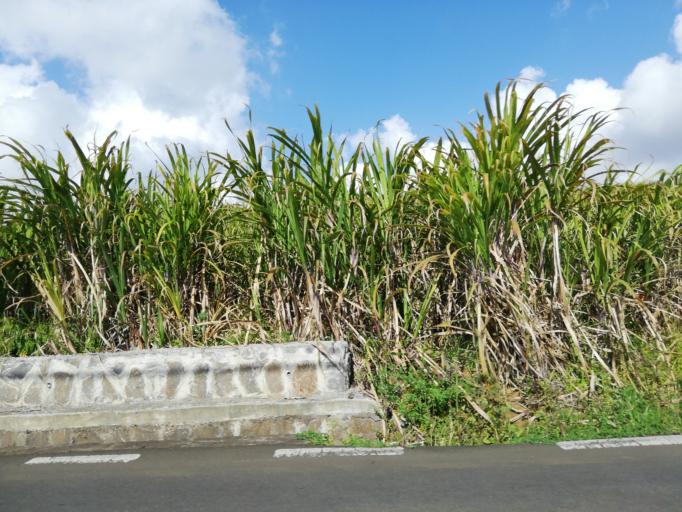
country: MU
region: Pamplemousses
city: Creve Coeur
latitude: -20.2036
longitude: 57.5698
